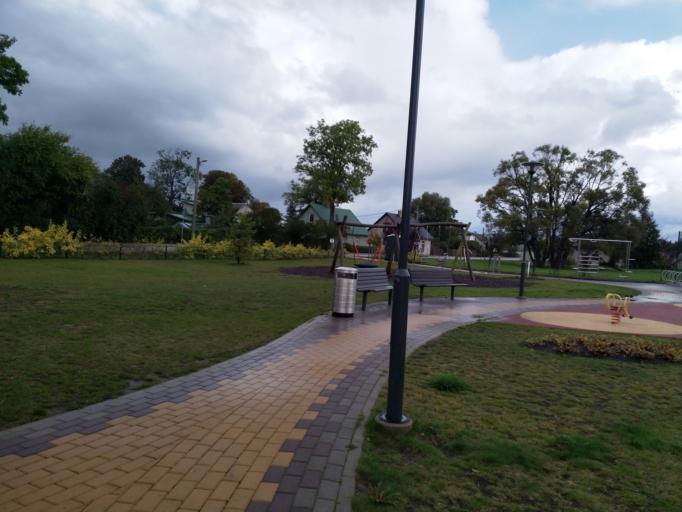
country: LV
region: Ventspils
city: Ventspils
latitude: 57.3742
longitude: 21.5889
